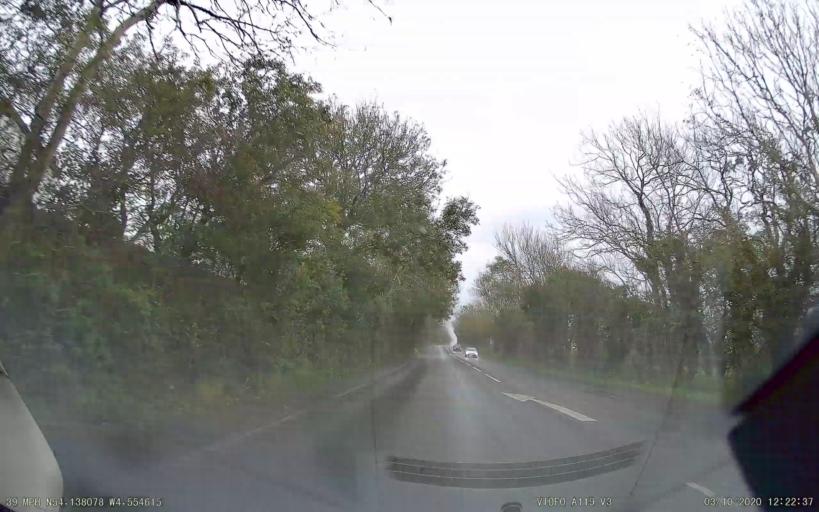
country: IM
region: Douglas
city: Douglas
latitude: 54.1381
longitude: -4.5546
